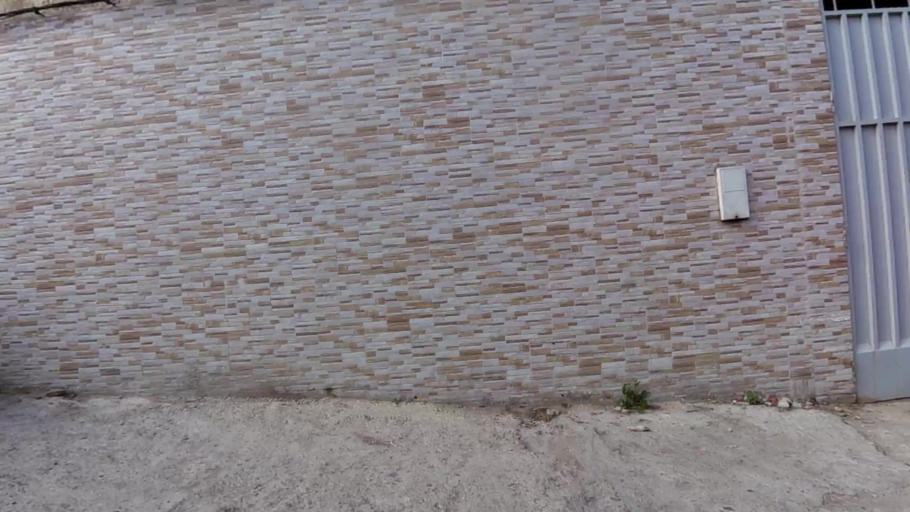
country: MA
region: Tanger-Tetouan
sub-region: Tanger-Assilah
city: Tangier
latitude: 35.7713
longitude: -5.7730
